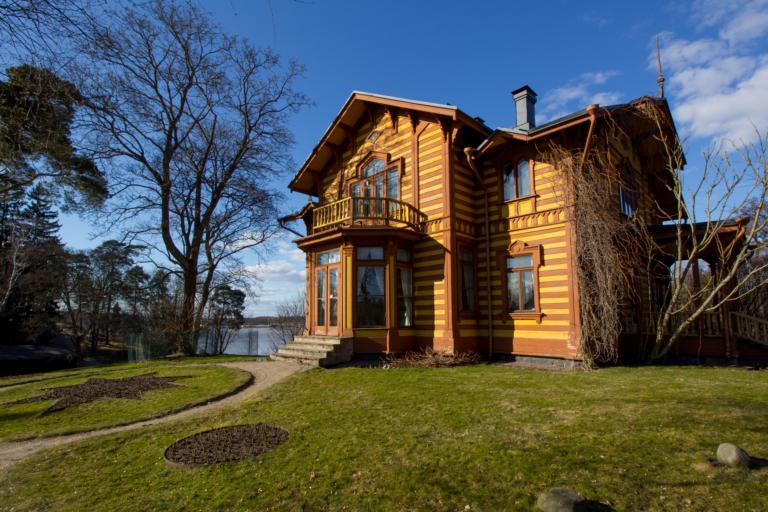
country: FI
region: Uusimaa
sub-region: Helsinki
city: Helsinki
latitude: 60.1808
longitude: 25.0343
